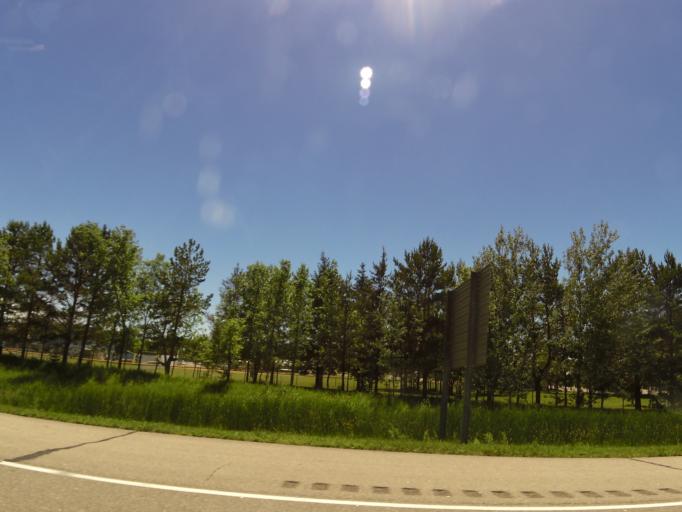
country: US
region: Minnesota
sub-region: Otter Tail County
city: New York Mills
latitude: 46.5243
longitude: -95.3762
